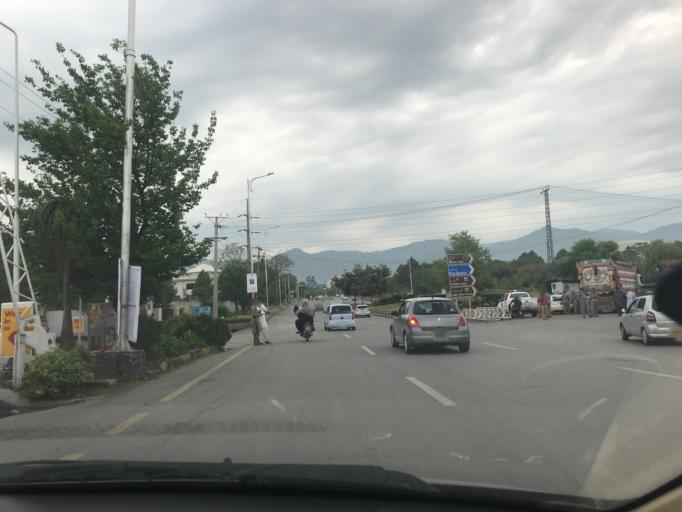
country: PK
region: Islamabad
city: Islamabad
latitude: 33.7086
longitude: 73.1052
